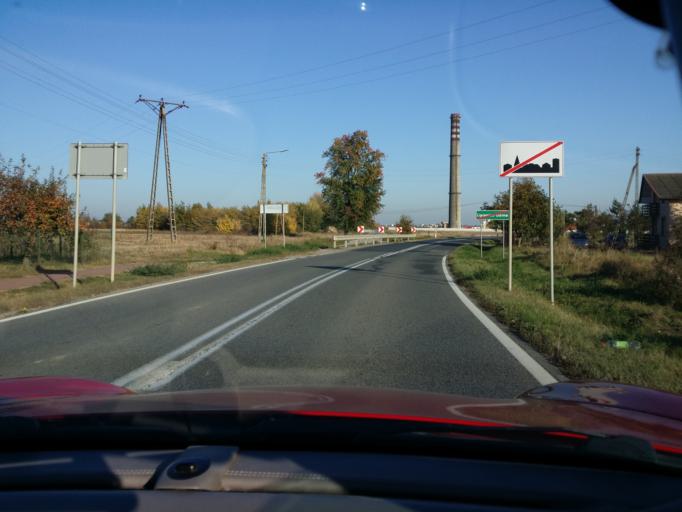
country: PL
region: Masovian Voivodeship
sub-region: Powiat szydlowiecki
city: Mirow
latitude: 51.2447
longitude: 21.0090
